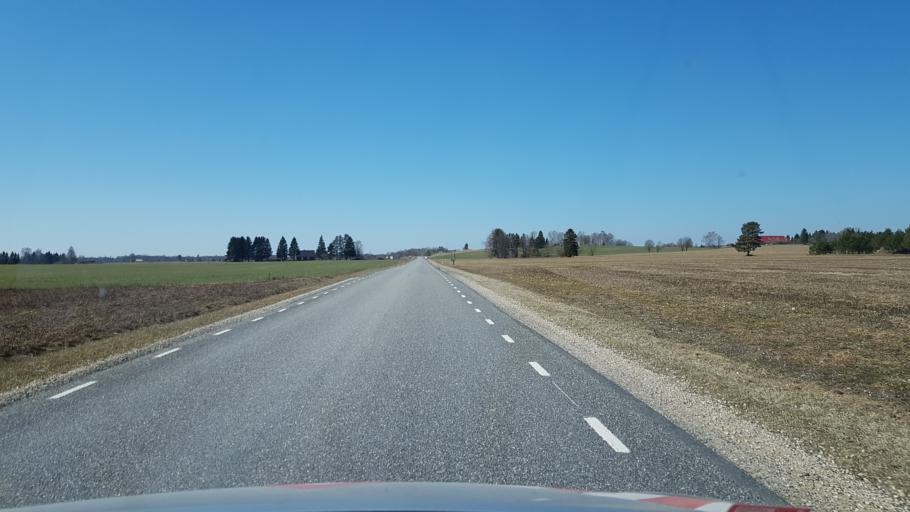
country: EE
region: Laeaene-Virumaa
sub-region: Rakke vald
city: Rakke
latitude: 59.0081
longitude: 26.1495
